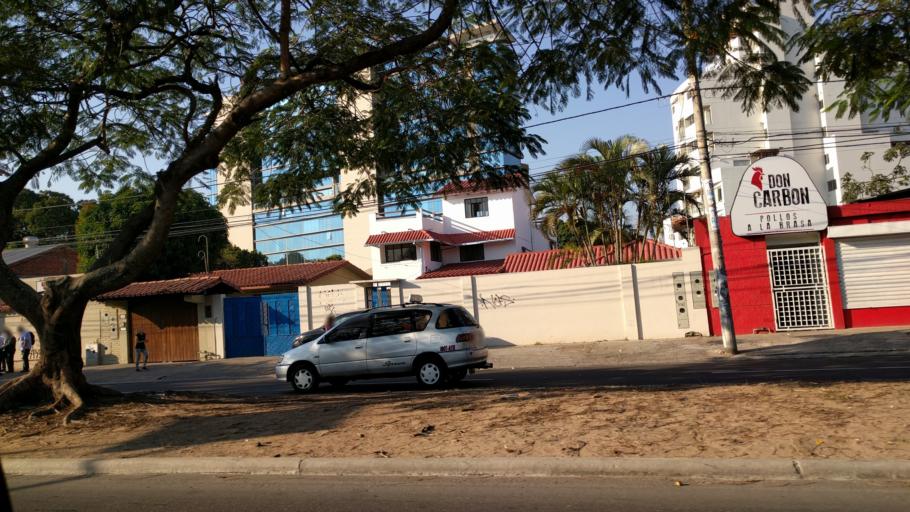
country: BO
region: Santa Cruz
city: Santa Cruz de la Sierra
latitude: -17.7705
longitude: -63.1808
